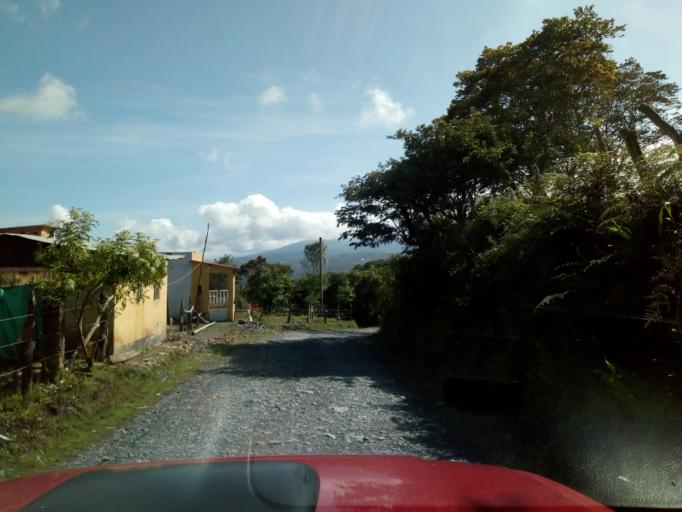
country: CO
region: Boyaca
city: Moniquira
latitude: 5.8854
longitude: -73.5409
